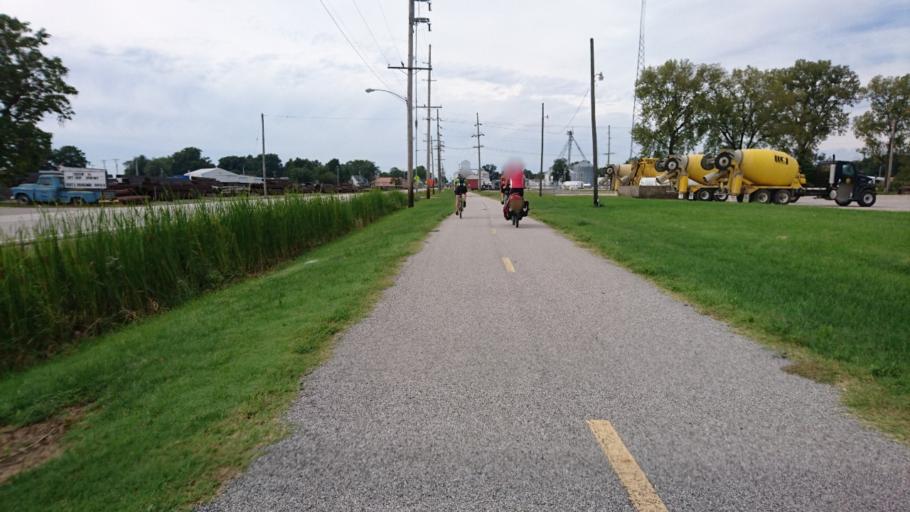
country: US
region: Illinois
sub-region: Madison County
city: Worden
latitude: 38.8924
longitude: -89.8412
